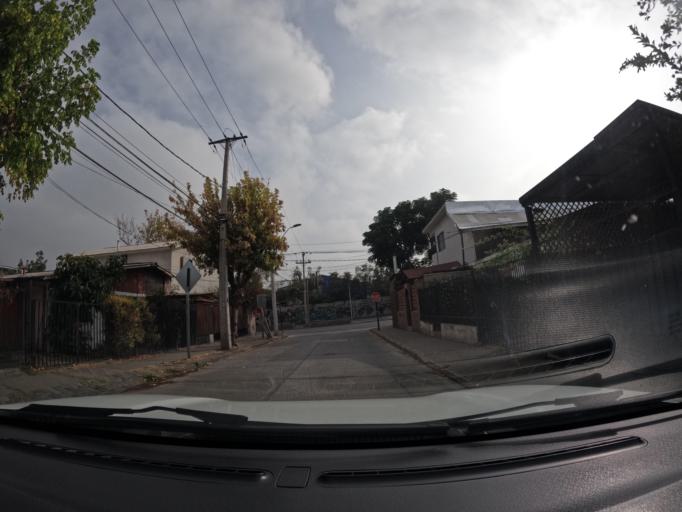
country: CL
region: Santiago Metropolitan
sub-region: Provincia de Santiago
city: Villa Presidente Frei, Nunoa, Santiago, Chile
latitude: -33.4704
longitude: -70.5494
